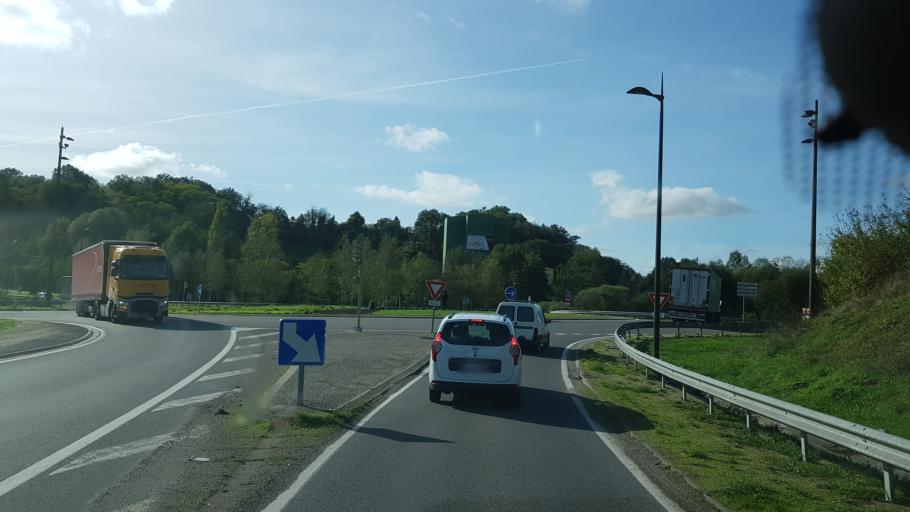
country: FR
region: Poitou-Charentes
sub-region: Departement de la Charente
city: Saint-Claud
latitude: 45.8894
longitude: 0.4720
